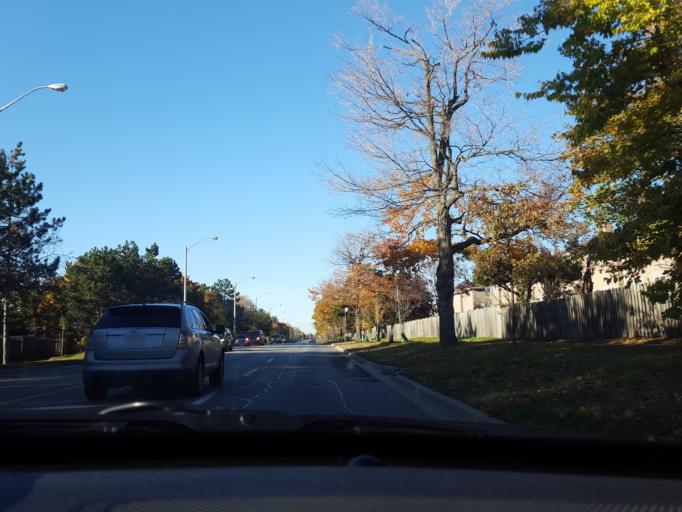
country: CA
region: Ontario
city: Scarborough
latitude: 43.8163
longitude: -79.2821
